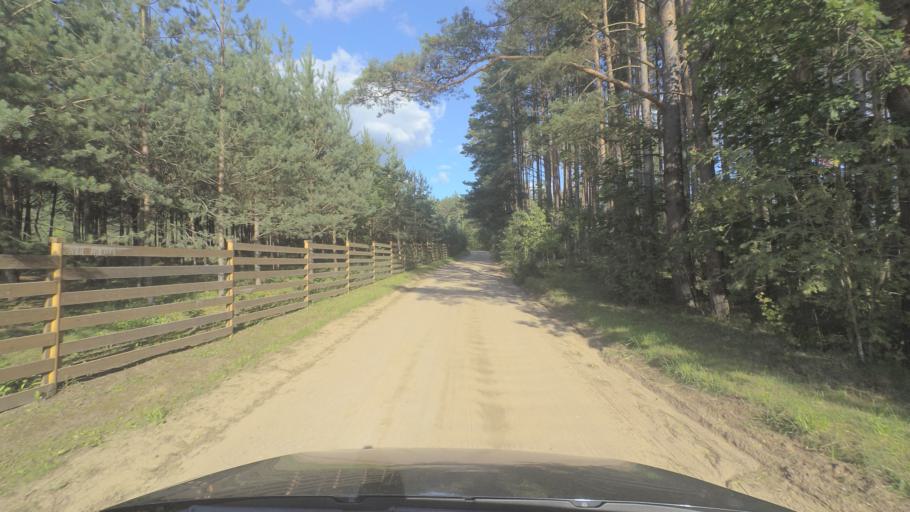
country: LT
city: Pabrade
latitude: 55.1395
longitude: 25.7144
